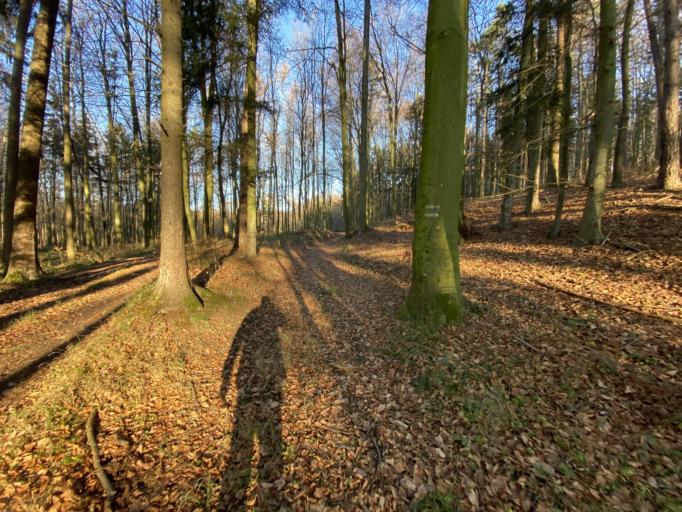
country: AT
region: Lower Austria
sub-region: Politischer Bezirk Sankt Polten
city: Boheimkirchen
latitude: 48.2022
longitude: 15.7190
